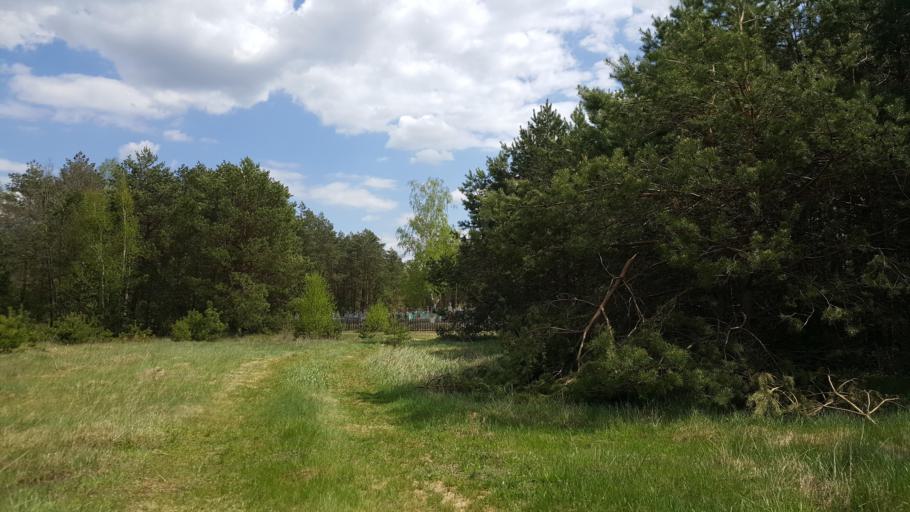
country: BY
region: Brest
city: Zhabinka
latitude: 52.4096
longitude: 24.0900
